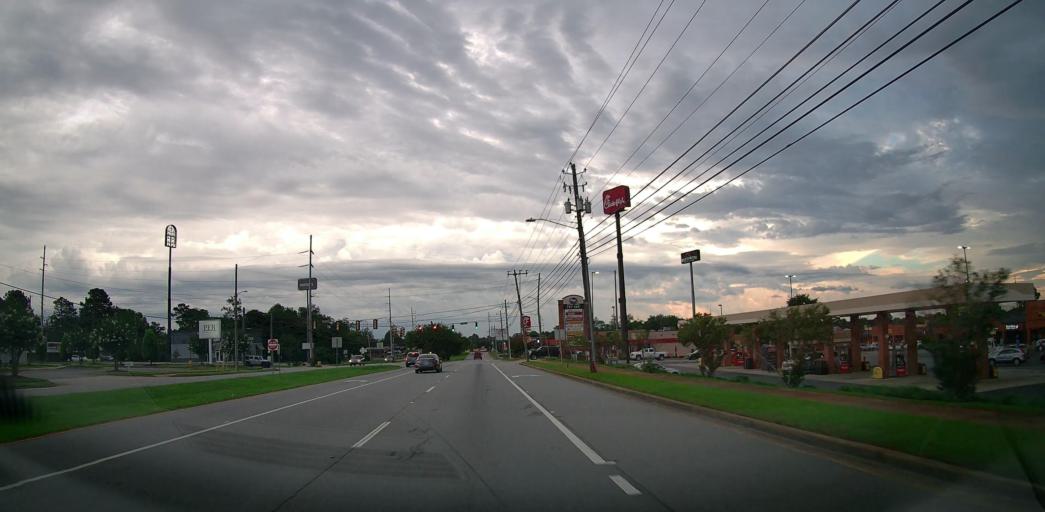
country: US
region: Georgia
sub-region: Houston County
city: Perry
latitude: 32.4683
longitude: -83.7406
